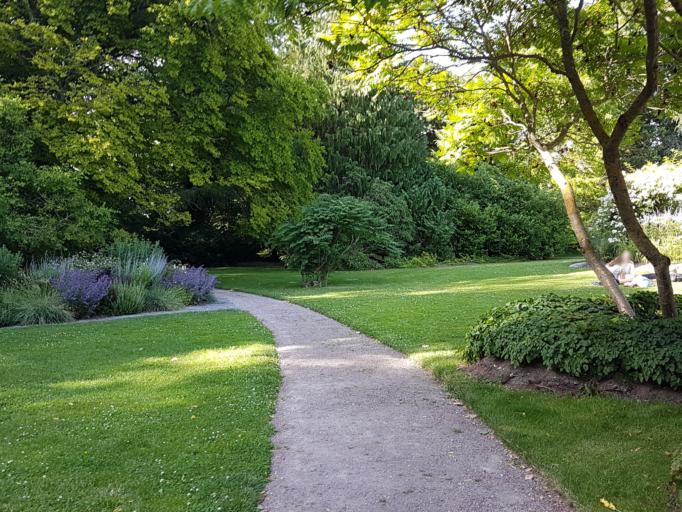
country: SE
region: Gotland
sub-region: Gotland
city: Visby
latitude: 57.6438
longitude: 18.2939
